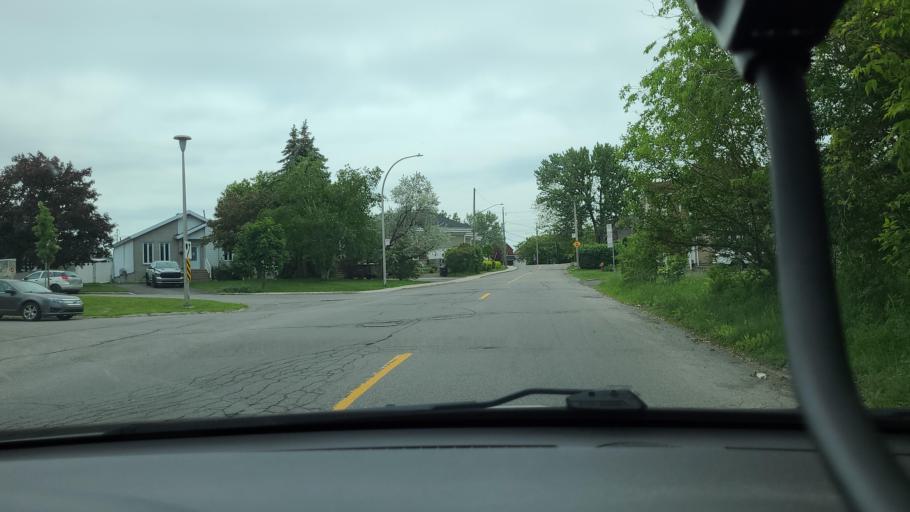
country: CA
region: Quebec
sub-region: Laurentides
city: Rosemere
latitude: 45.6252
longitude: -73.7749
